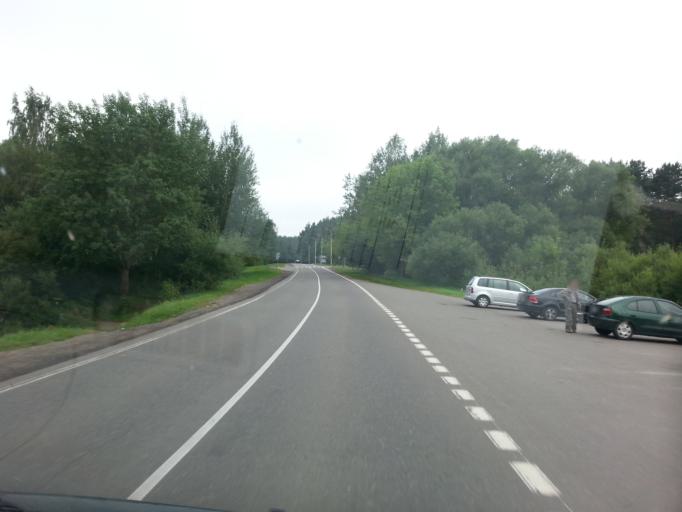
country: BY
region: Minsk
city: Syomkava
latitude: 53.9878
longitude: 27.4584
